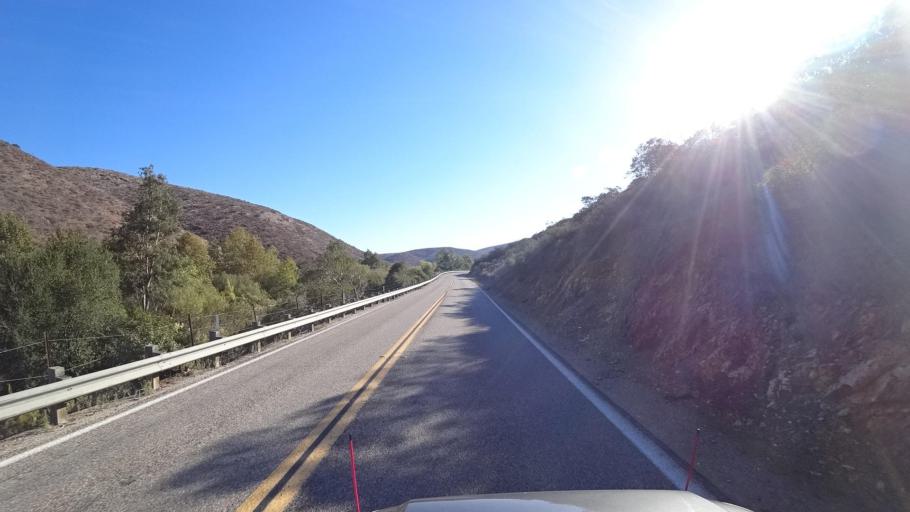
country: US
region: California
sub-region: San Diego County
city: Jamul
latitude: 32.6403
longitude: -116.8804
